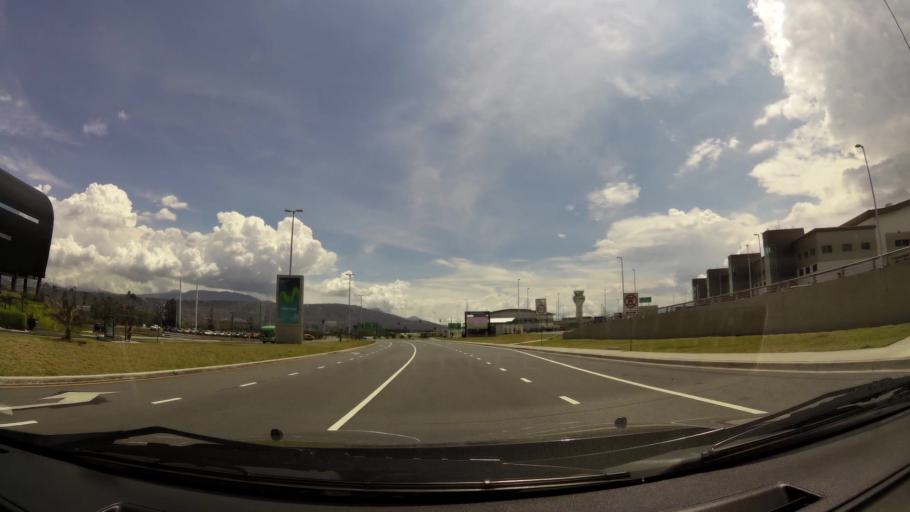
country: EC
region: Pichincha
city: Quito
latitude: -0.1315
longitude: -78.3592
